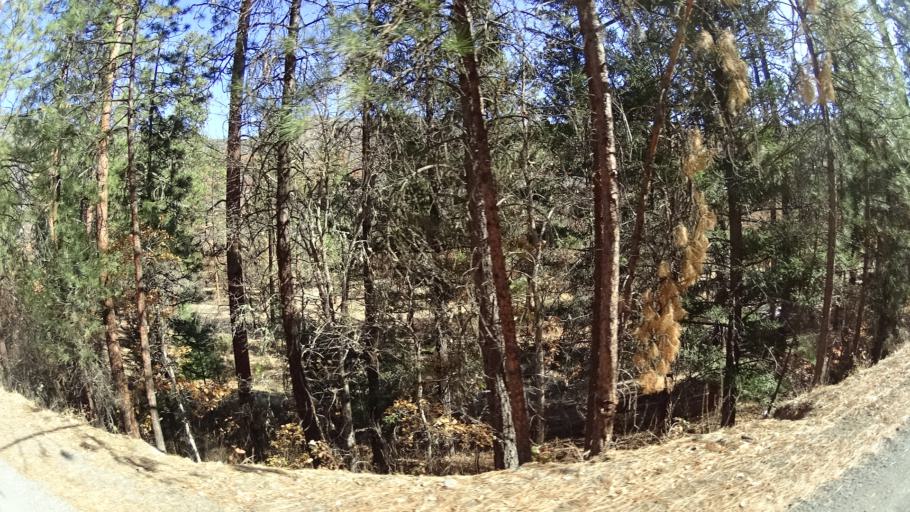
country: US
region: California
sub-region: Siskiyou County
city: Yreka
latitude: 41.8618
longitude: -122.7073
